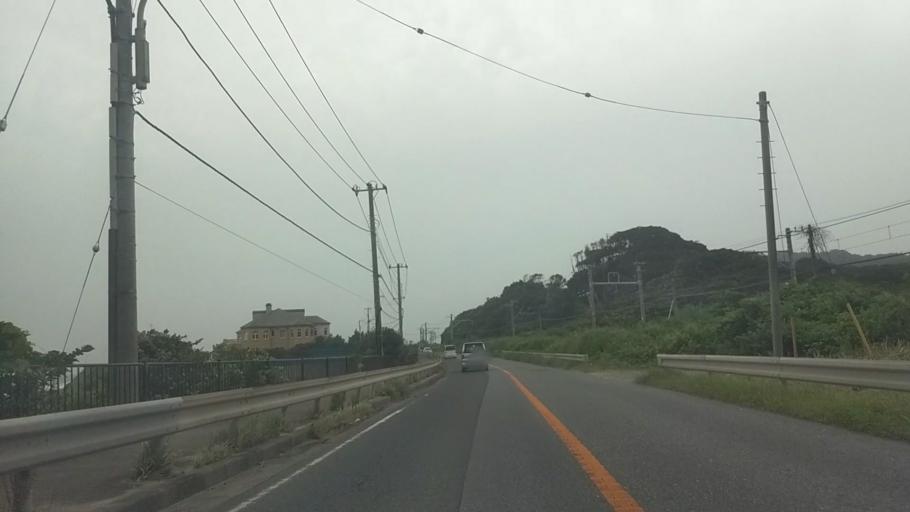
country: JP
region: Chiba
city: Futtsu
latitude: 35.1806
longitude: 139.8193
